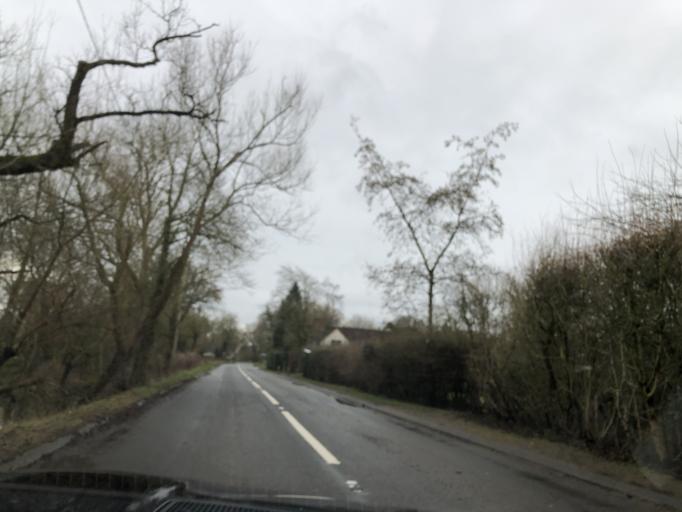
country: GB
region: England
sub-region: Warwickshire
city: Wroxall
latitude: 52.2902
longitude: -1.7119
